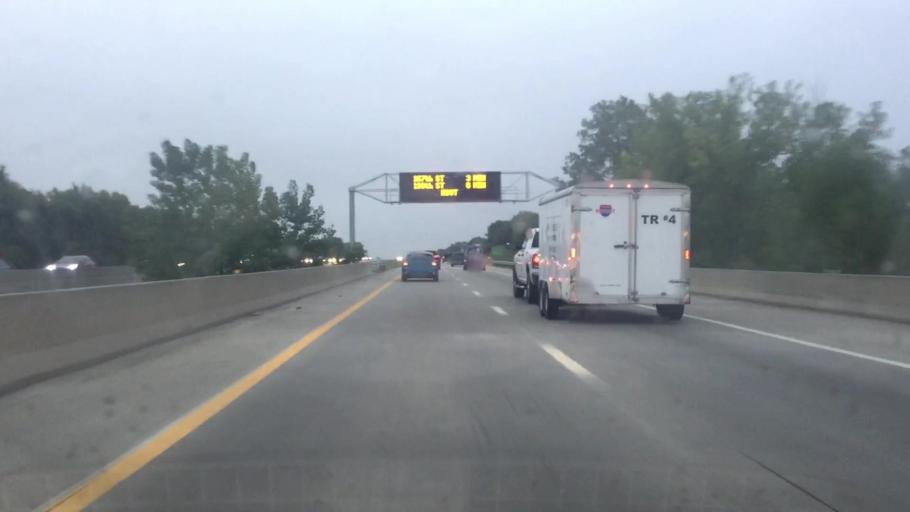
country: US
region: Kansas
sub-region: Johnson County
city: Lenexa
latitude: 38.8693
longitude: -94.6769
